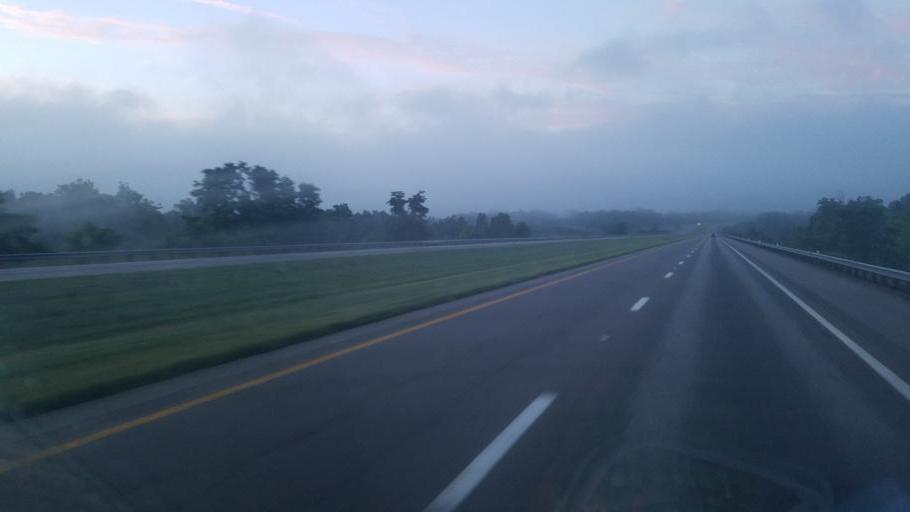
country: US
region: Ohio
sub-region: Pike County
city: Waverly
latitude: 39.2232
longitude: -82.8292
